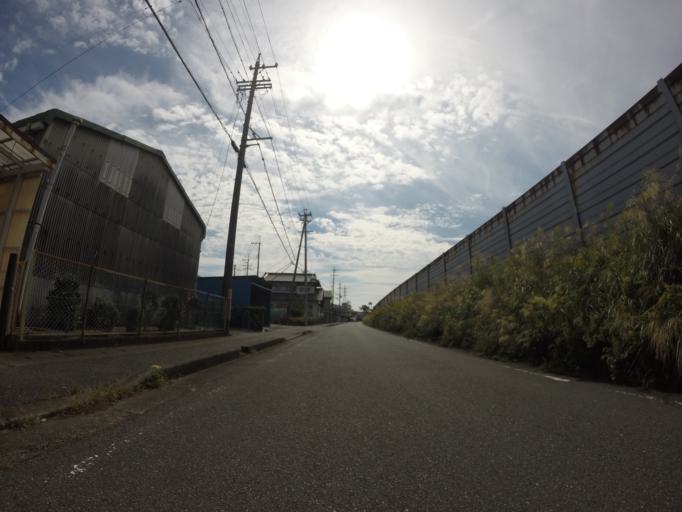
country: JP
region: Shizuoka
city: Fuji
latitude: 35.1197
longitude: 138.6236
